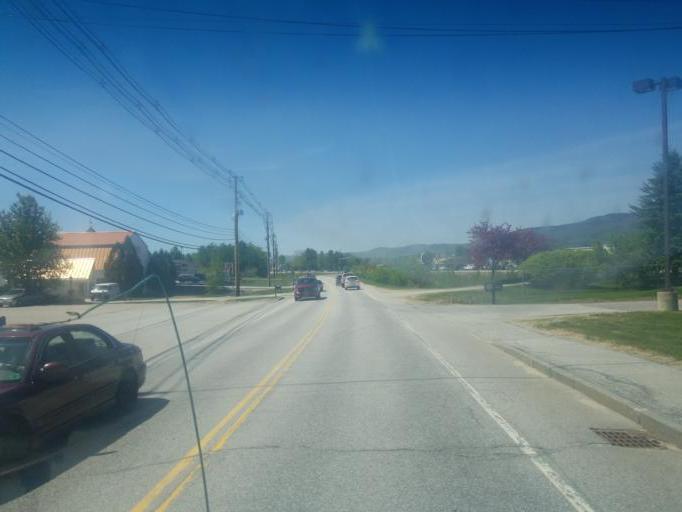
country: US
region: New Hampshire
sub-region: Grafton County
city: Plymouth
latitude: 43.7696
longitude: -71.7196
